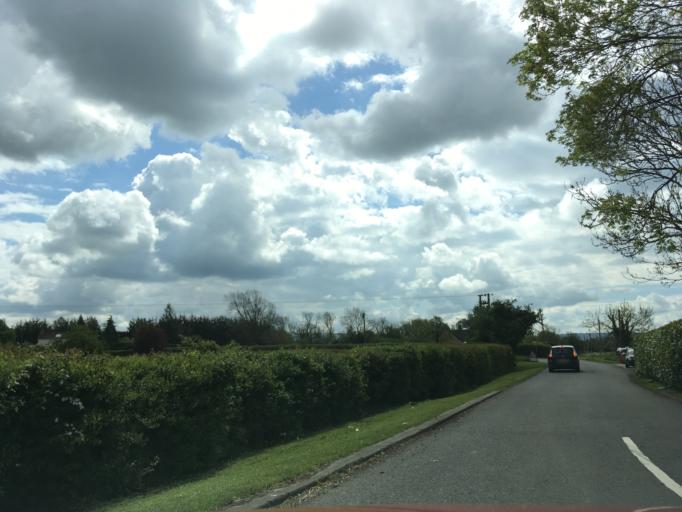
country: GB
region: England
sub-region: Gloucestershire
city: Stonehouse
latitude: 51.7812
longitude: -2.3165
